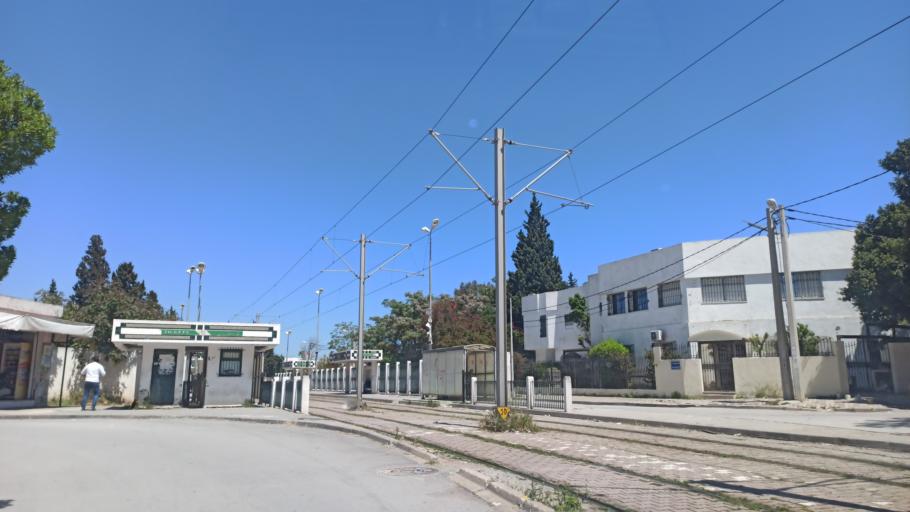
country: TN
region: Tunis
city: Tunis
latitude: 36.8229
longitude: 10.1853
